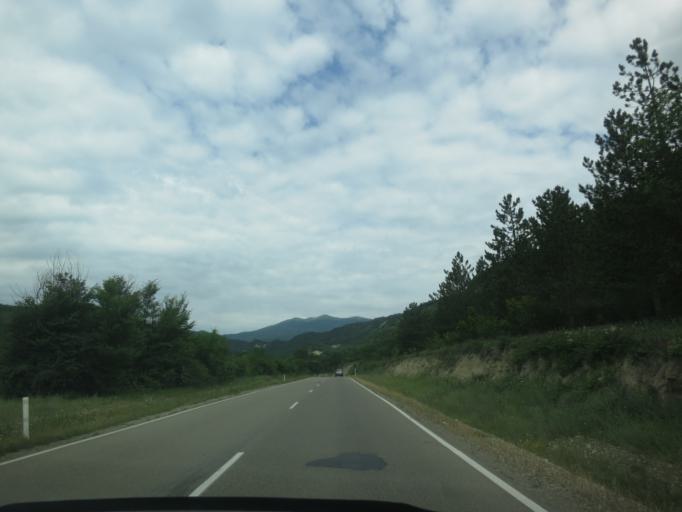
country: GE
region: Kakheti
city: Sagarejo
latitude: 41.8022
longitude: 45.1538
